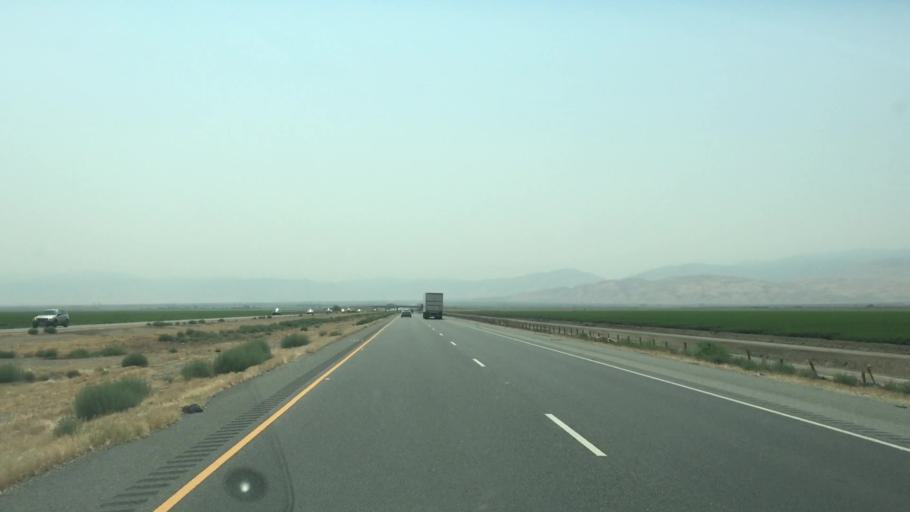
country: US
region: California
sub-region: Kern County
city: Greenfield
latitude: 35.1378
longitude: -119.0847
